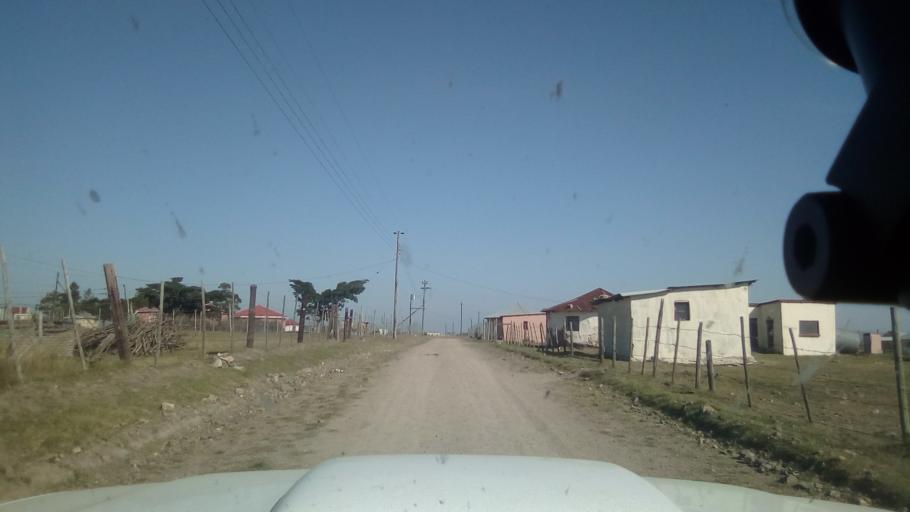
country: ZA
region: Eastern Cape
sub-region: Buffalo City Metropolitan Municipality
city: Bhisho
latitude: -32.9410
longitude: 27.3375
